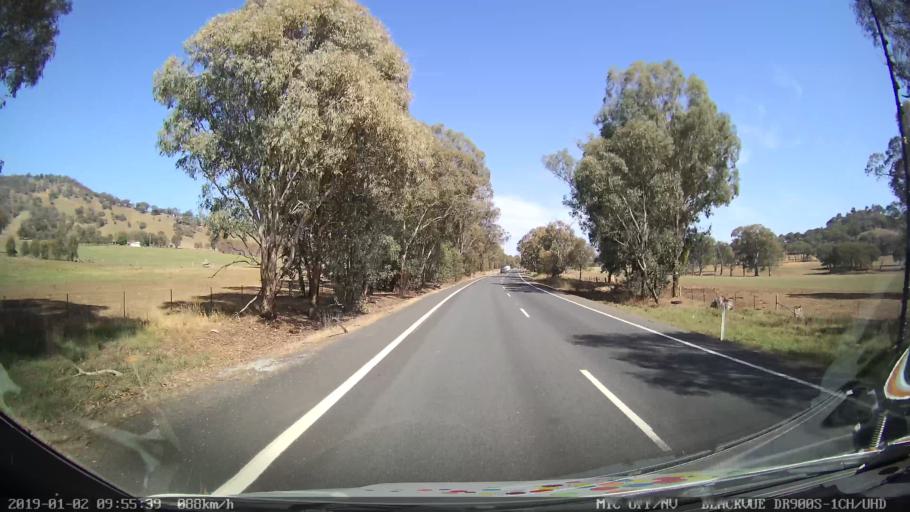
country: AU
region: New South Wales
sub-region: Tumut Shire
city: Tumut
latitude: -35.2219
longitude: 148.1857
